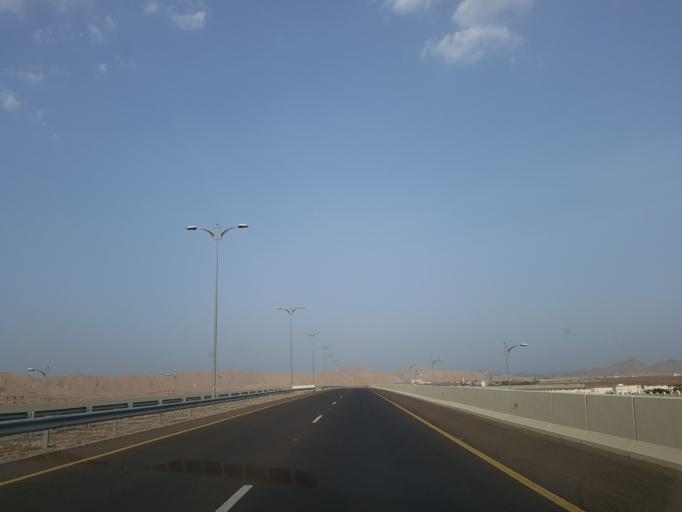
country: OM
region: Al Buraimi
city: Al Buraymi
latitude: 24.2374
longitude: 55.9070
